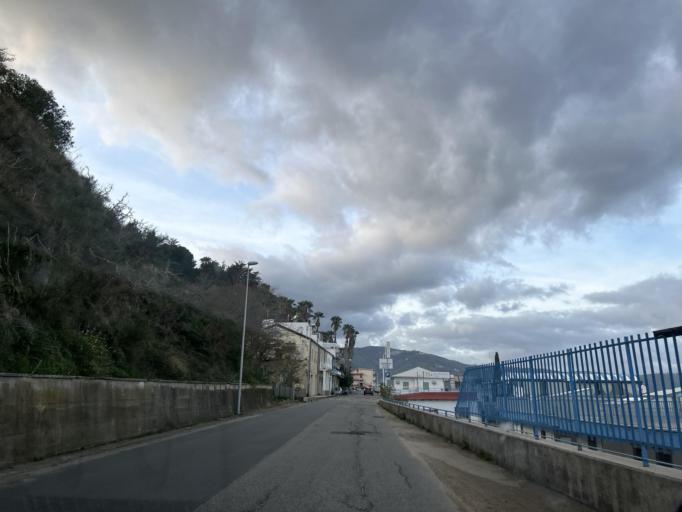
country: IT
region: Calabria
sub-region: Provincia di Catanzaro
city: Soverato Marina
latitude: 38.6943
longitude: 16.5443
